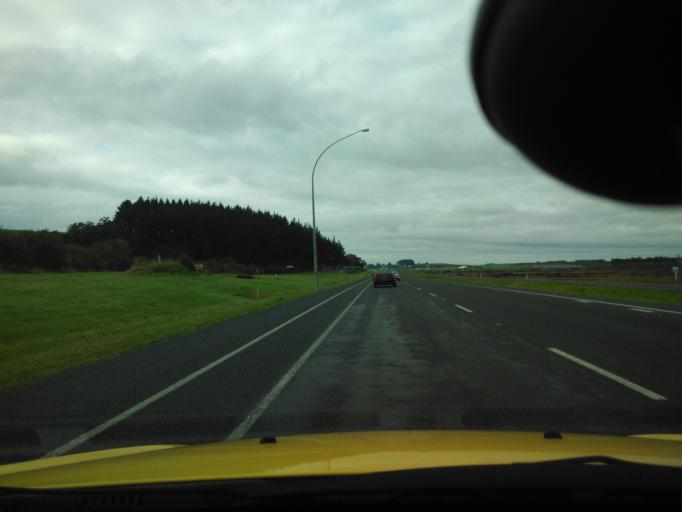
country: NZ
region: Waikato
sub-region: Waikato District
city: Te Kauwhata
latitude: -37.3402
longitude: 175.0643
